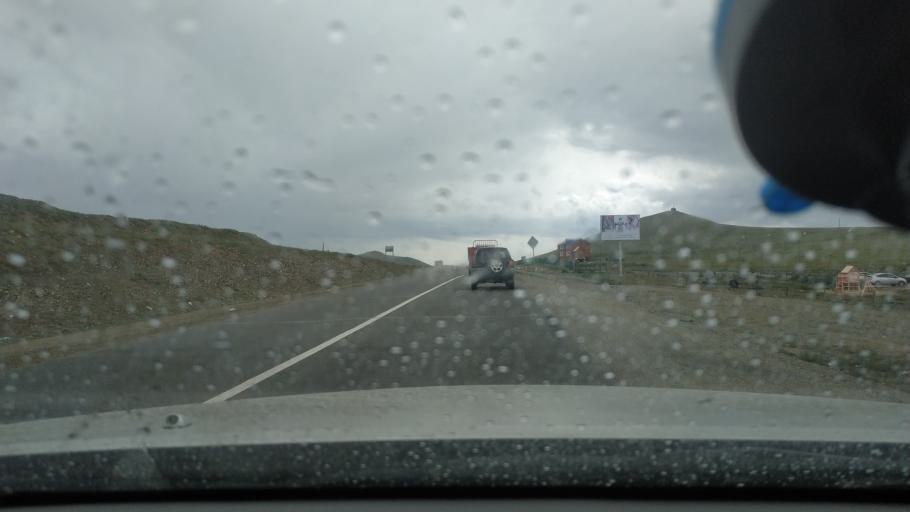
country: MN
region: Ulaanbaatar
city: Ulaanbaatar
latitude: 47.7911
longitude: 106.7459
